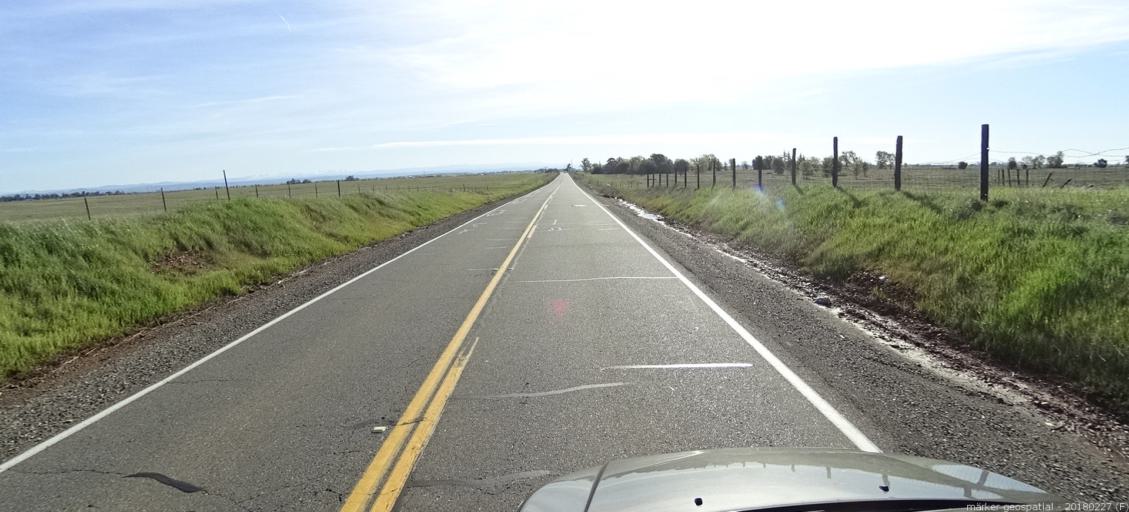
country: US
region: California
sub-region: Sacramento County
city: Vineyard
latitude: 38.4962
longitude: -121.2863
